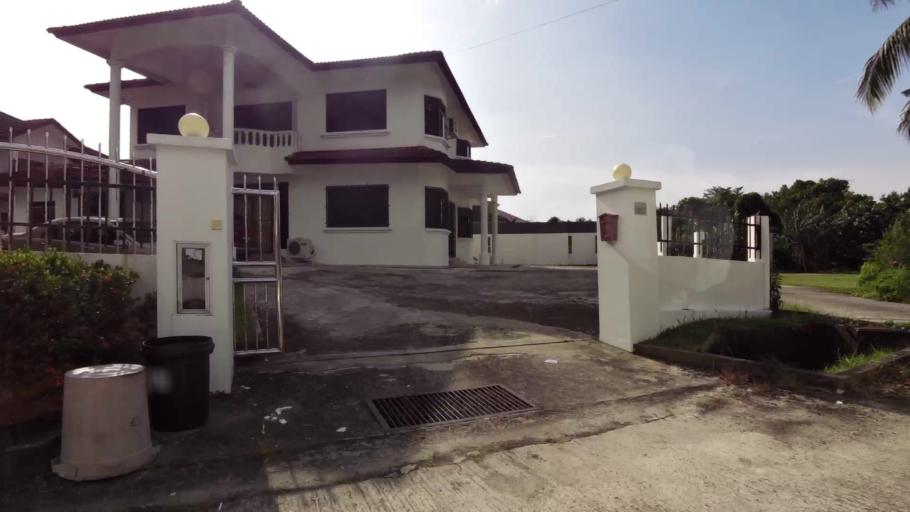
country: BN
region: Brunei and Muara
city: Bandar Seri Begawan
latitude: 4.9622
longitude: 114.9702
